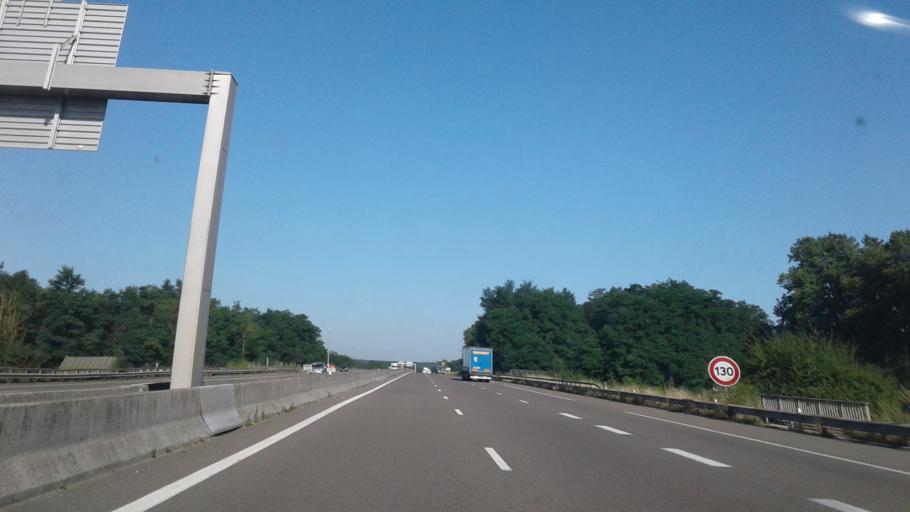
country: FR
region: Rhone-Alpes
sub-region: Departement de l'Ain
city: Saint-Martin-du-Mont
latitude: 46.0738
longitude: 5.3139
